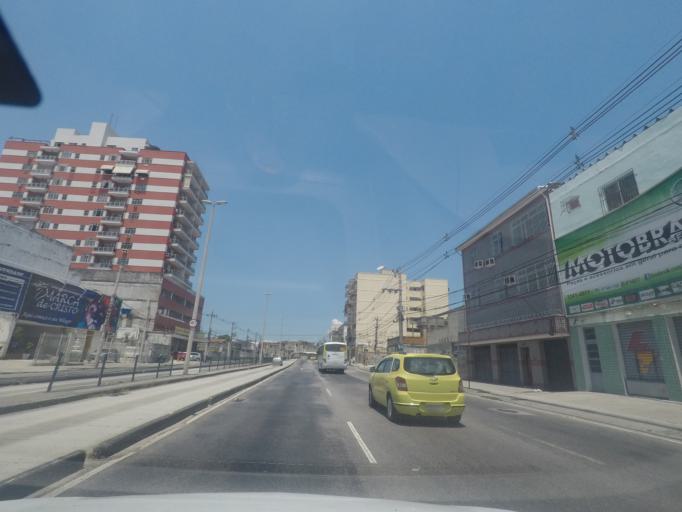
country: BR
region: Rio de Janeiro
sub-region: Duque De Caxias
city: Duque de Caxias
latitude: -22.8381
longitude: -43.2923
